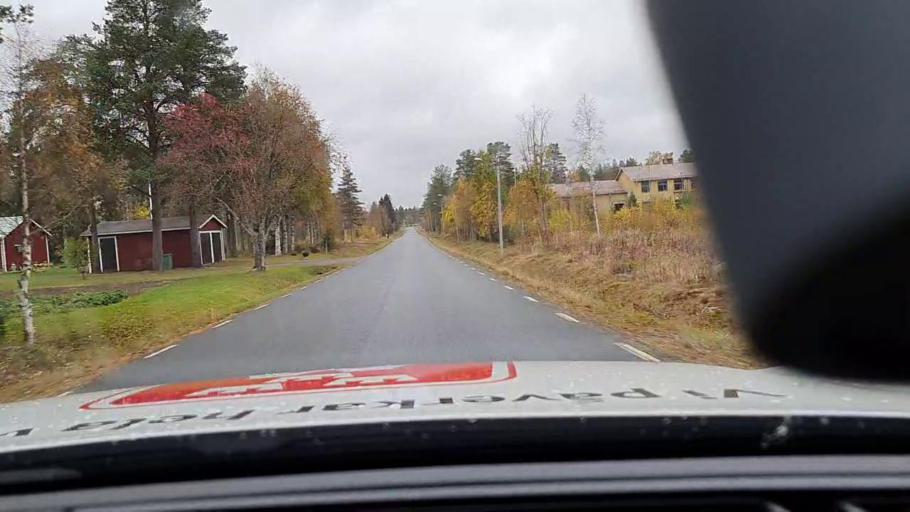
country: SE
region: Norrbotten
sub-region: Haparanda Kommun
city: Haparanda
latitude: 65.9433
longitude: 23.8007
